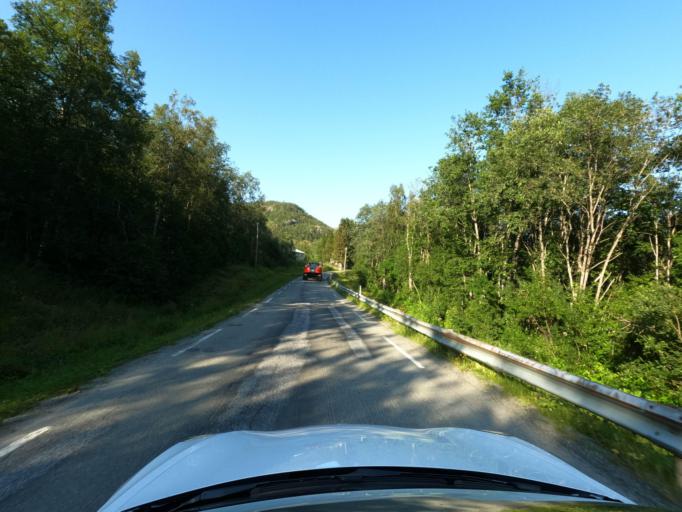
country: NO
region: Nordland
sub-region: Narvik
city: Bjerkvik
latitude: 68.5548
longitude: 17.6014
